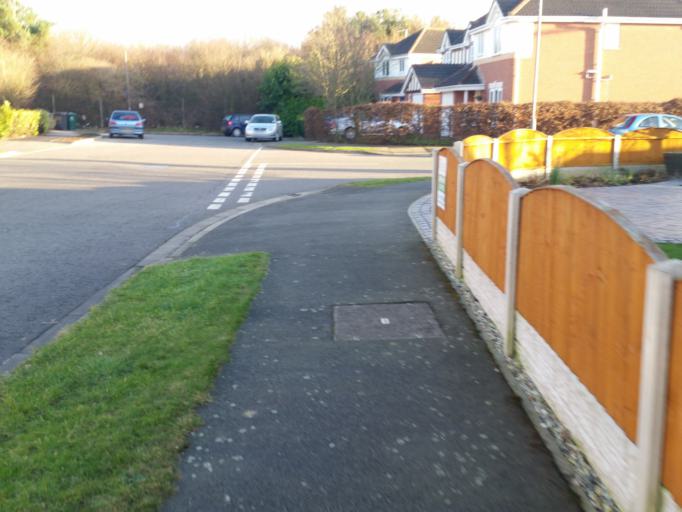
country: GB
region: England
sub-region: Derbyshire
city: Borrowash
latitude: 52.8826
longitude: -1.4113
